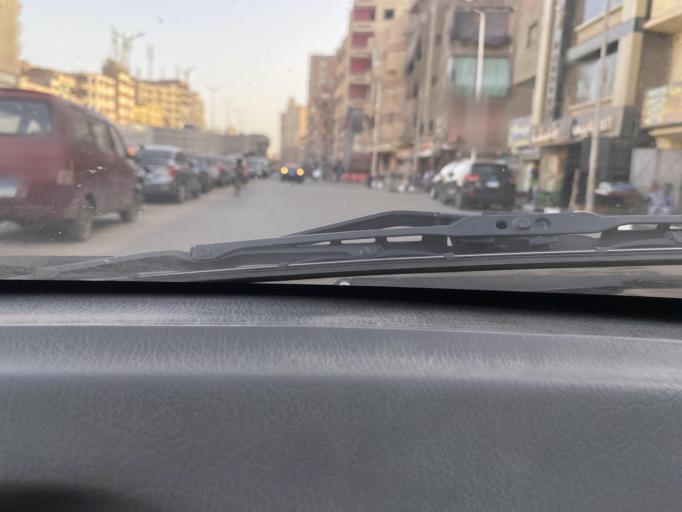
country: EG
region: Muhafazat al Qahirah
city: Cairo
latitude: 30.1229
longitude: 31.2970
